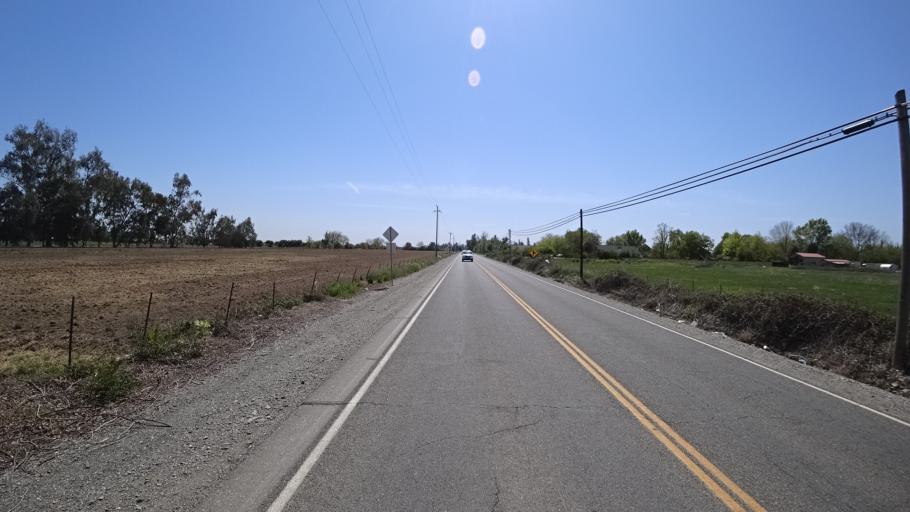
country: US
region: California
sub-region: Glenn County
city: Orland
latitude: 39.7236
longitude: -122.1970
